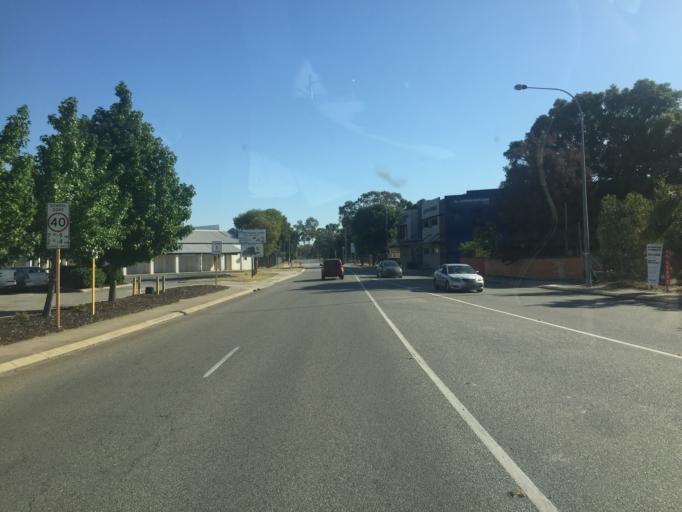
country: AU
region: Western Australia
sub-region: Gosnells
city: Kenwick
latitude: -32.0371
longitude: 115.9684
